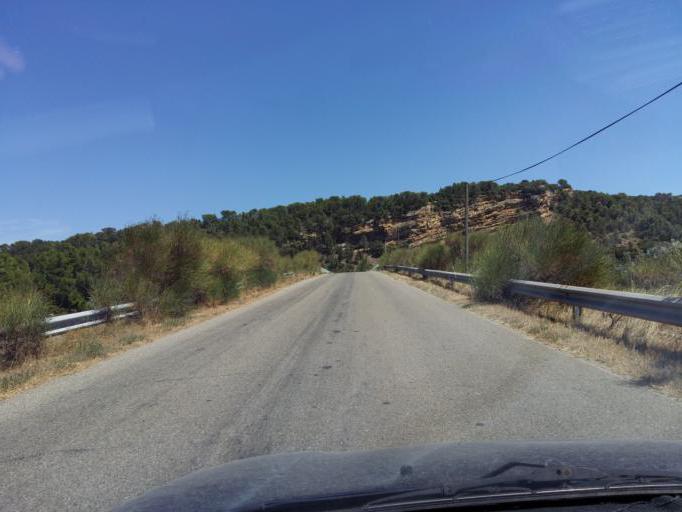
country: FR
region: Provence-Alpes-Cote d'Azur
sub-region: Departement du Vaucluse
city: Piolenc
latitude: 44.1725
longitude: 4.7579
